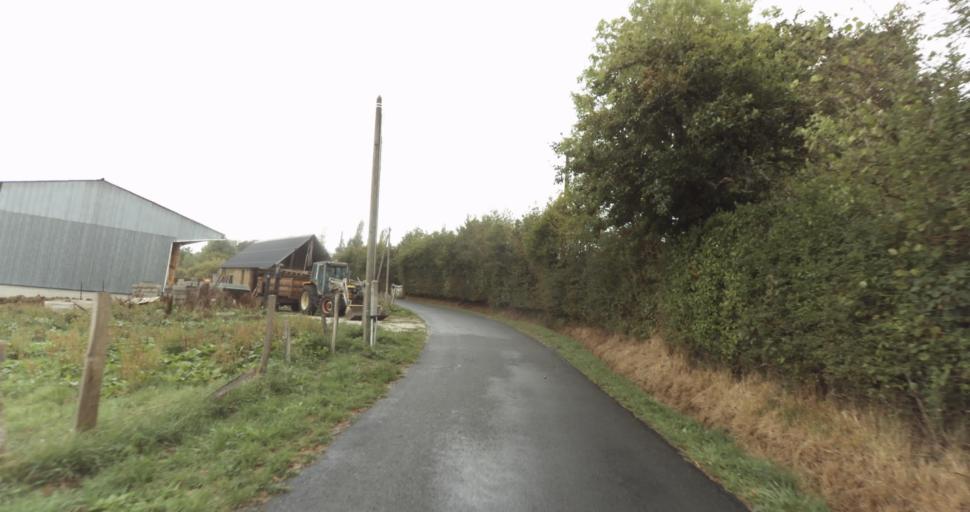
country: FR
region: Lower Normandy
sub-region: Departement de l'Orne
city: Sainte-Gauburge-Sainte-Colombe
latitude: 48.7510
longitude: 0.4700
